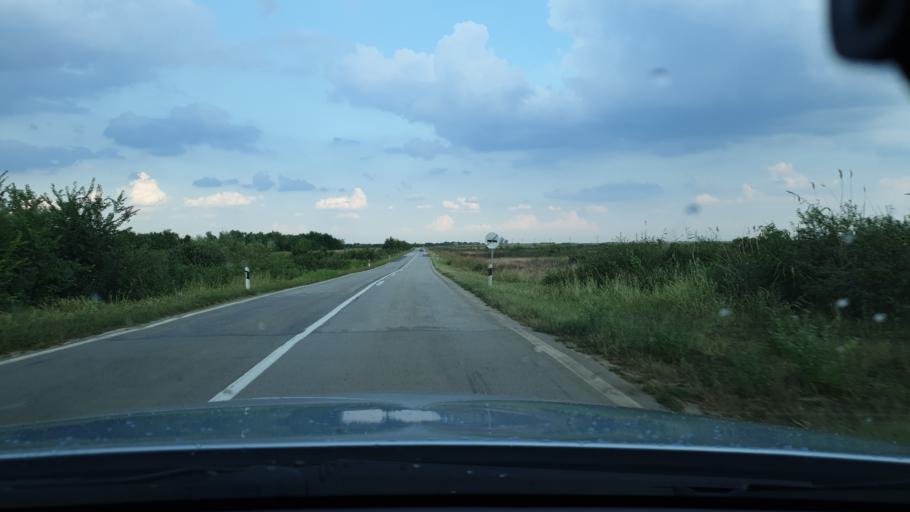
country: RS
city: Boka
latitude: 45.3488
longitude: 20.7988
